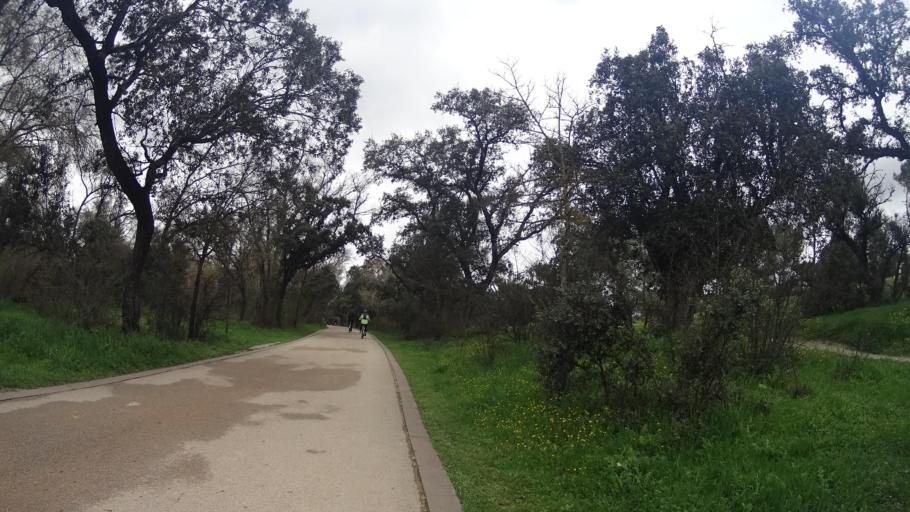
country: ES
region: Madrid
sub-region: Provincia de Madrid
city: Latina
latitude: 40.4057
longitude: -3.7675
